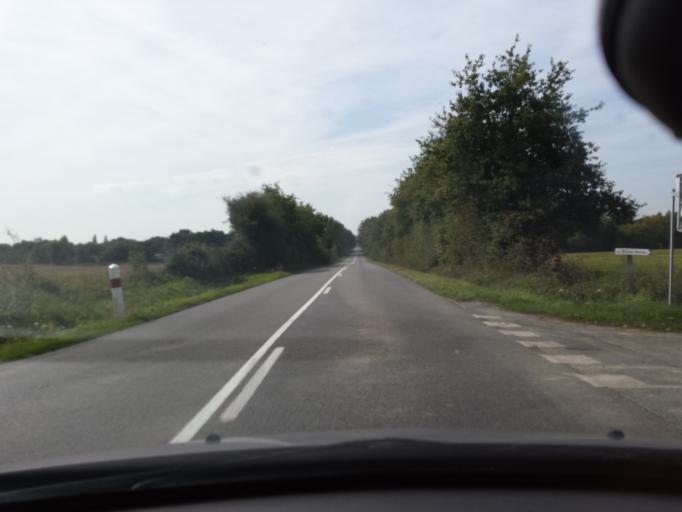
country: FR
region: Pays de la Loire
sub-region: Departement de la Vendee
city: Nieul-le-Dolent
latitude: 46.5829
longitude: -1.4862
